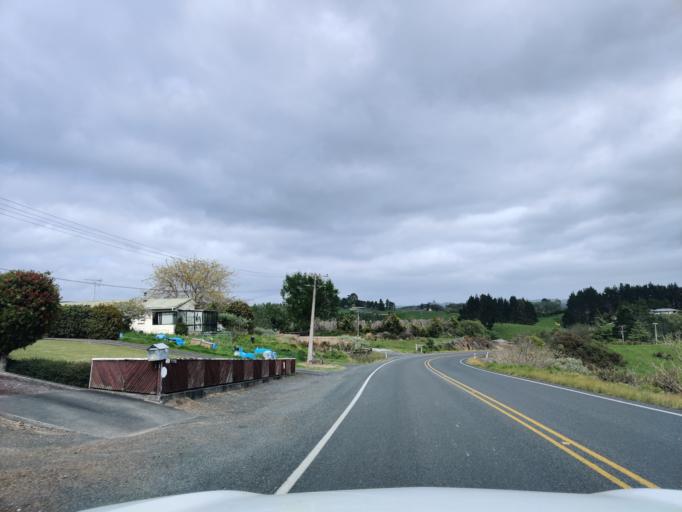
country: NZ
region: Waikato
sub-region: Waikato District
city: Ngaruawahia
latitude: -37.5778
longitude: 175.1336
